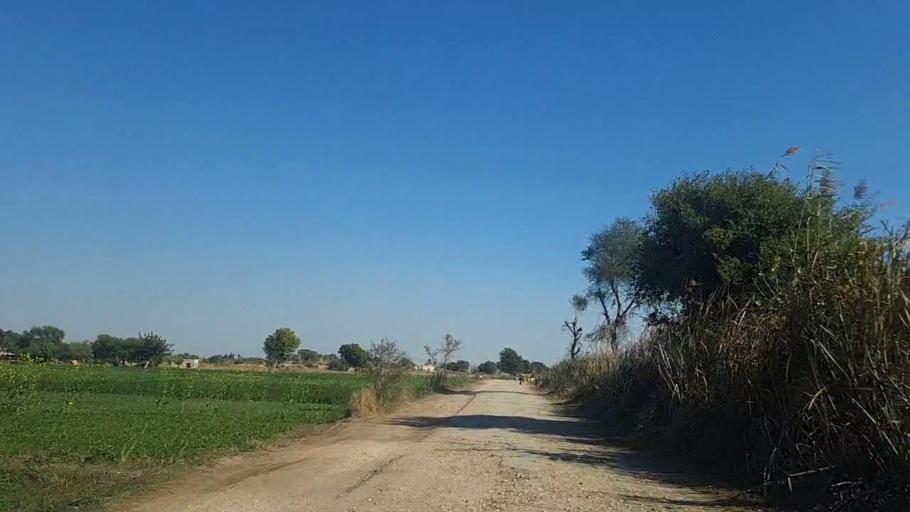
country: PK
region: Sindh
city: Sanghar
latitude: 26.2091
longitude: 68.9197
